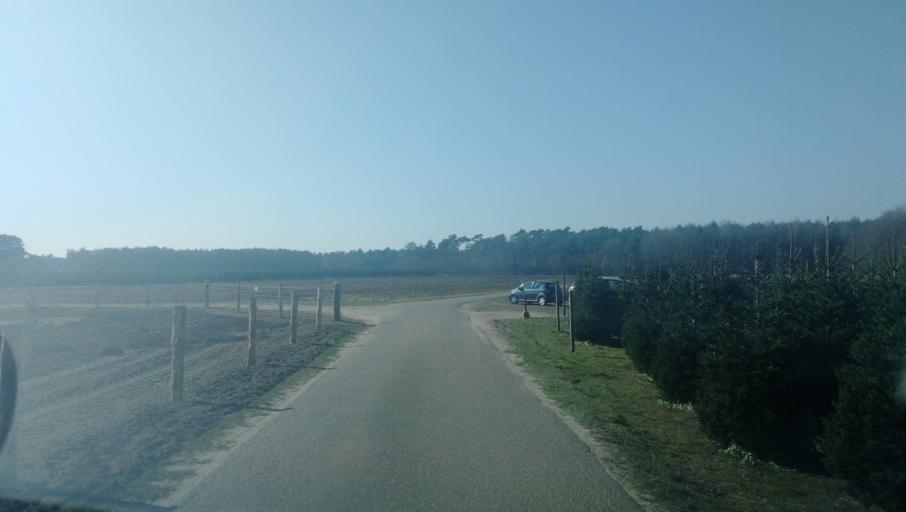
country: NL
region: Limburg
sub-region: Gemeente Venlo
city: Tegelen
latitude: 51.3835
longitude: 6.0982
